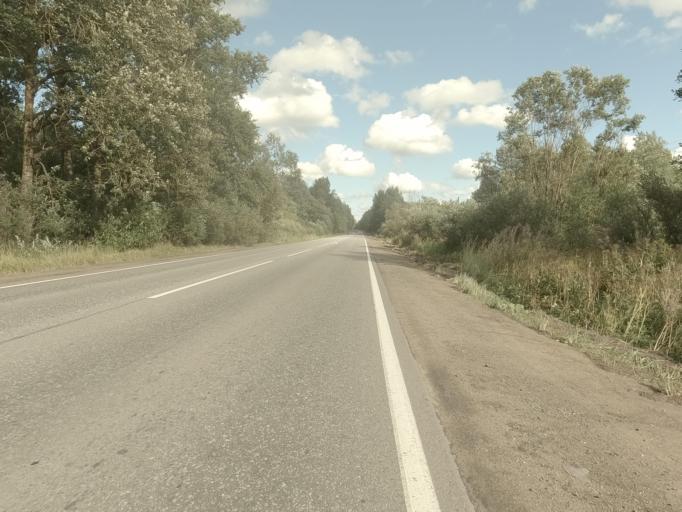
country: RU
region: Leningrad
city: Romanovka
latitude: 60.0237
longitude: 30.7067
